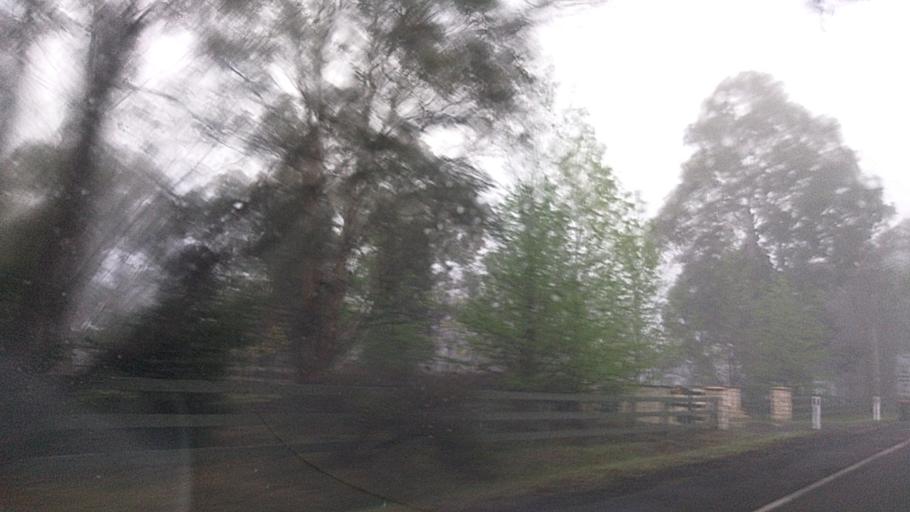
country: AU
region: New South Wales
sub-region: Wollondilly
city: Douglas Park
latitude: -34.2485
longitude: 150.7258
